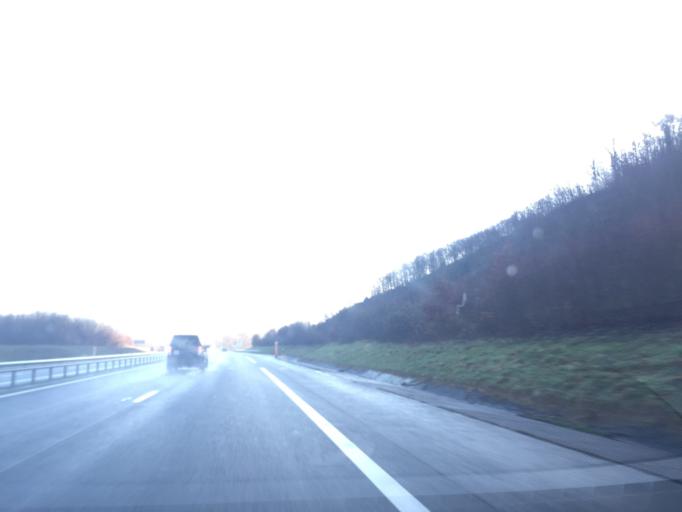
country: FR
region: Limousin
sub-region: Departement de la Correze
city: Saint-Pantaleon-de-Larche
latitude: 45.1639
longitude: 1.4500
